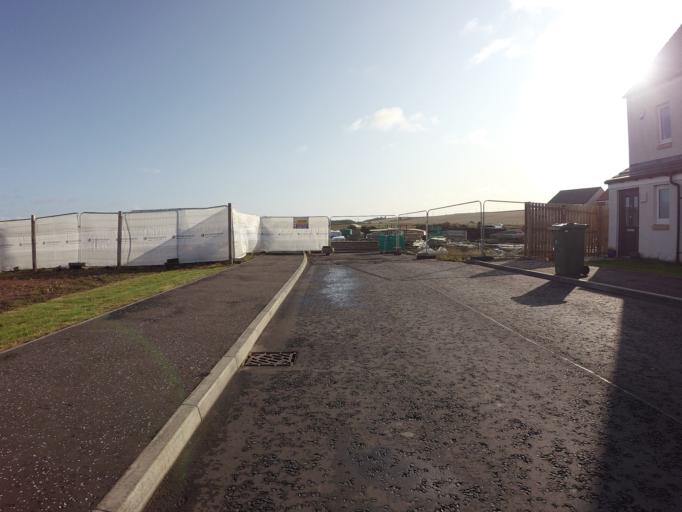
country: GB
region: Scotland
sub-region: East Lothian
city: Prestonpans
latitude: 55.9408
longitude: -3.0023
